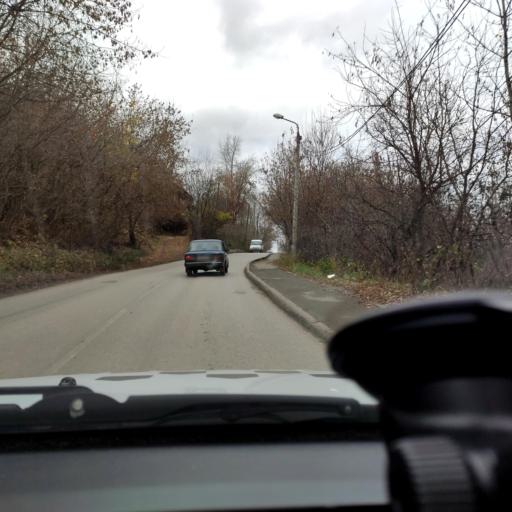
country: RU
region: Perm
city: Perm
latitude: 58.0296
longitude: 56.3137
